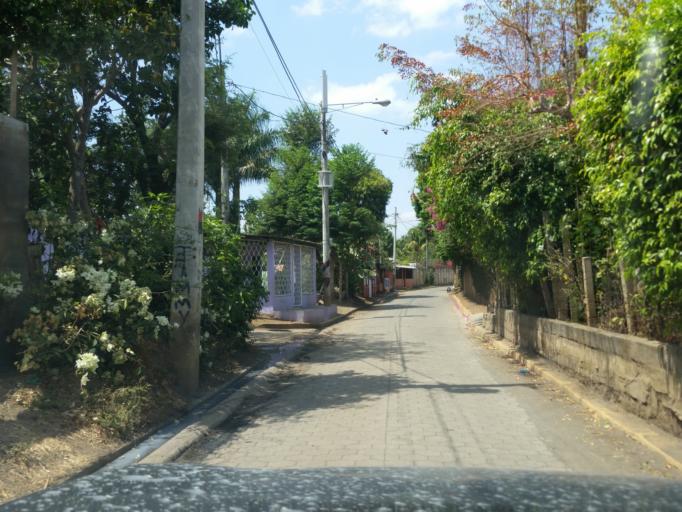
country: NI
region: Masaya
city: Ticuantepe
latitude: 12.0675
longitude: -86.2111
